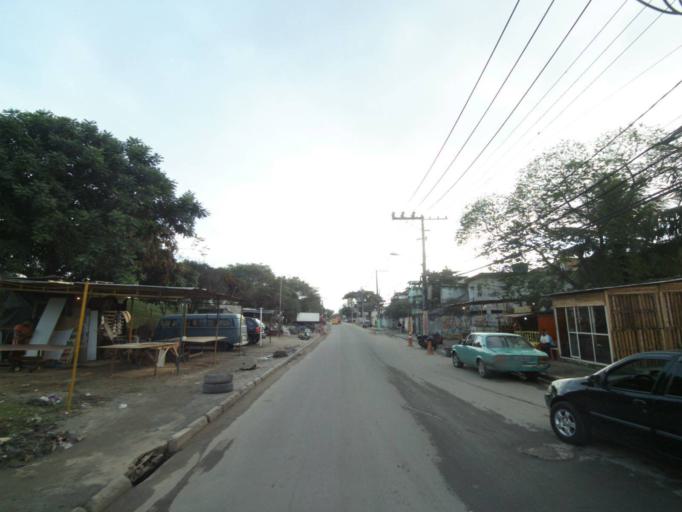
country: BR
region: Rio de Janeiro
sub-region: Nilopolis
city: Nilopolis
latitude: -22.8555
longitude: -43.4933
